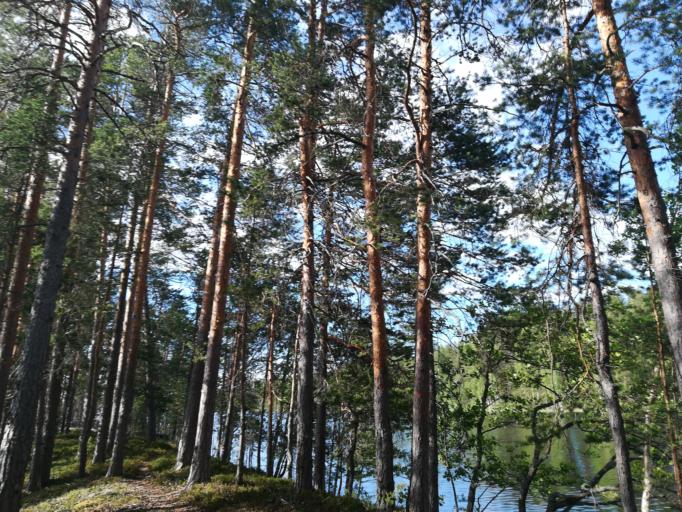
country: FI
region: Southern Savonia
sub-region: Savonlinna
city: Savonlinna
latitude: 61.6444
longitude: 28.7084
